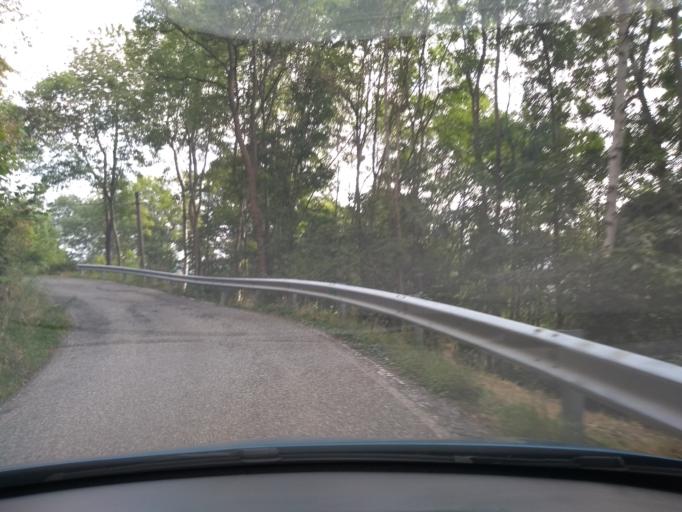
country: IT
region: Piedmont
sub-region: Provincia di Torino
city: Corio
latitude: 45.3057
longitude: 7.5093
